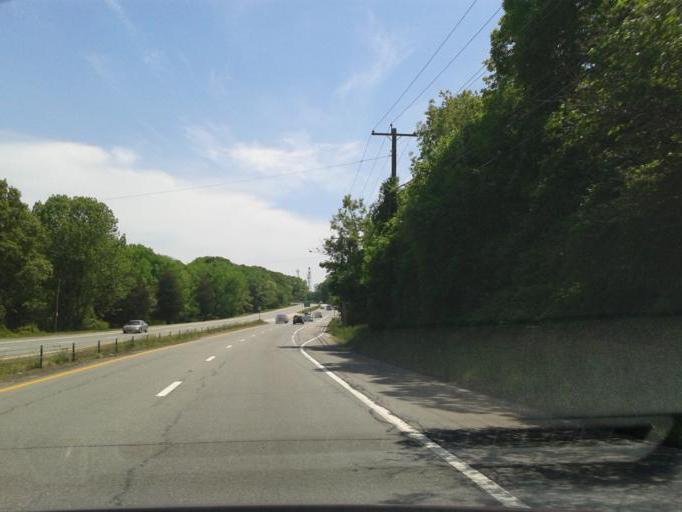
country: US
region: Rhode Island
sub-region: Washington County
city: North Kingstown
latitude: 41.5081
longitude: -71.4599
